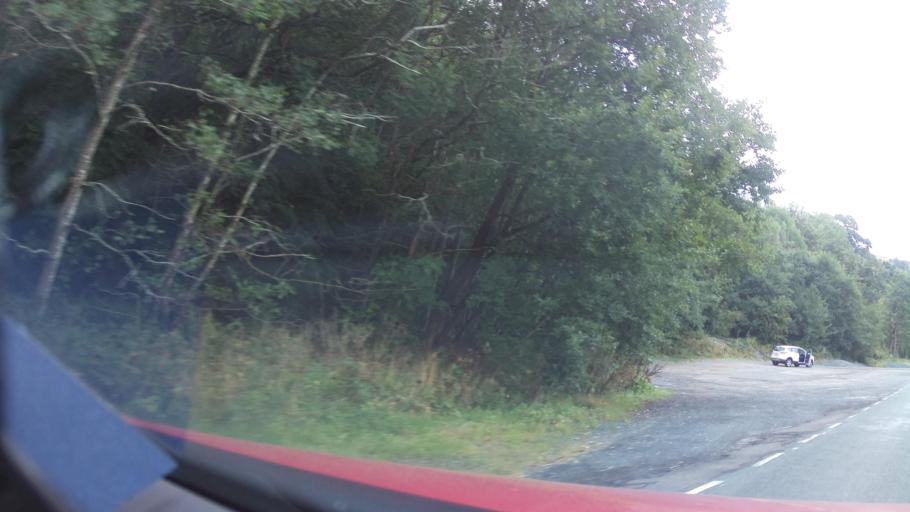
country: GB
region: England
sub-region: North Yorkshire
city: Leyburn
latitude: 54.3919
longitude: -1.8278
